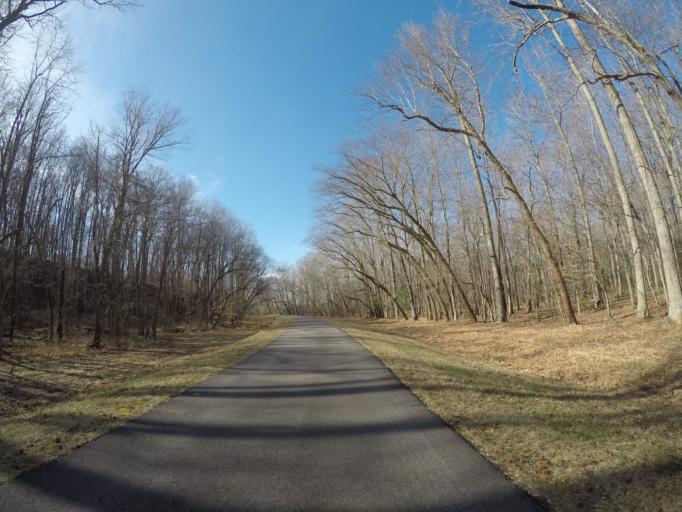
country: US
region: Maryland
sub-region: Charles County
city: Bennsville
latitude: 38.5965
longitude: -77.0351
